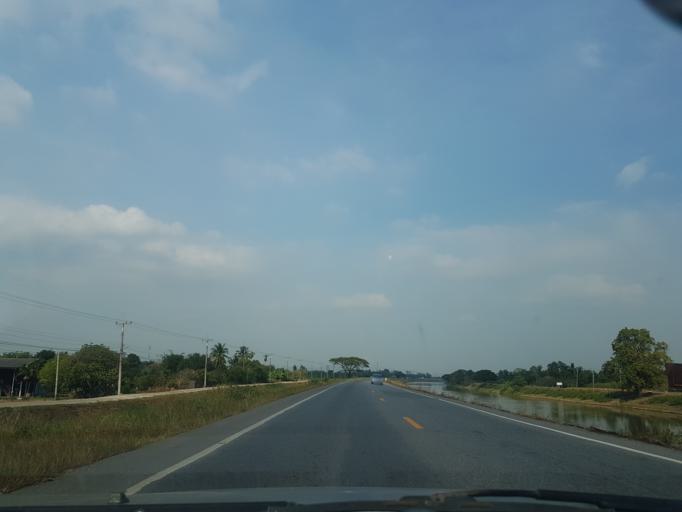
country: TH
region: Phra Nakhon Si Ayutthaya
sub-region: Amphoe Tha Ruea
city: Tha Ruea
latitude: 14.5219
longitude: 100.7389
